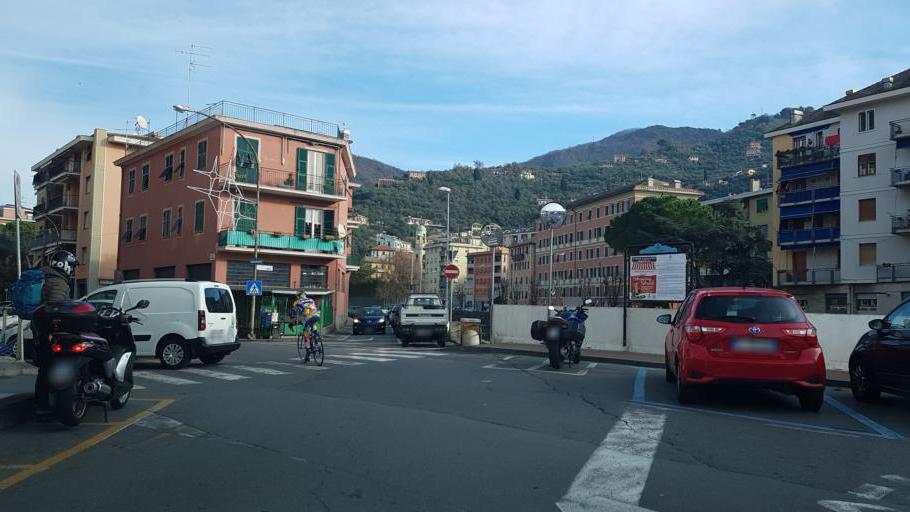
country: IT
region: Liguria
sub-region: Provincia di Genova
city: Recco
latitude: 44.3634
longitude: 9.1440
